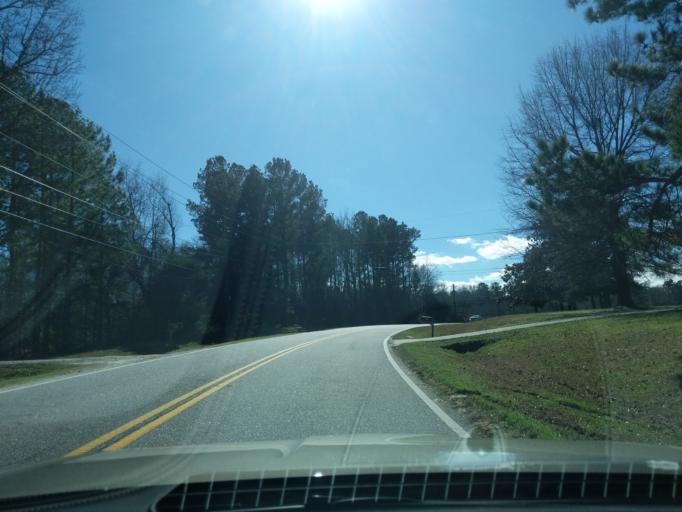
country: US
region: Georgia
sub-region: Columbia County
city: Evans
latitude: 33.5419
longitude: -82.1644
